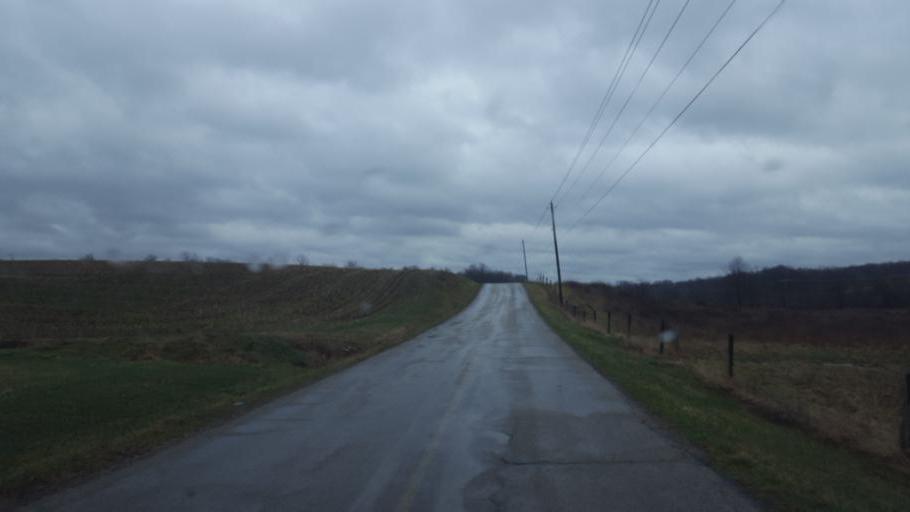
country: US
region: Ohio
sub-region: Sandusky County
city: Bellville
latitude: 40.5634
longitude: -82.5257
